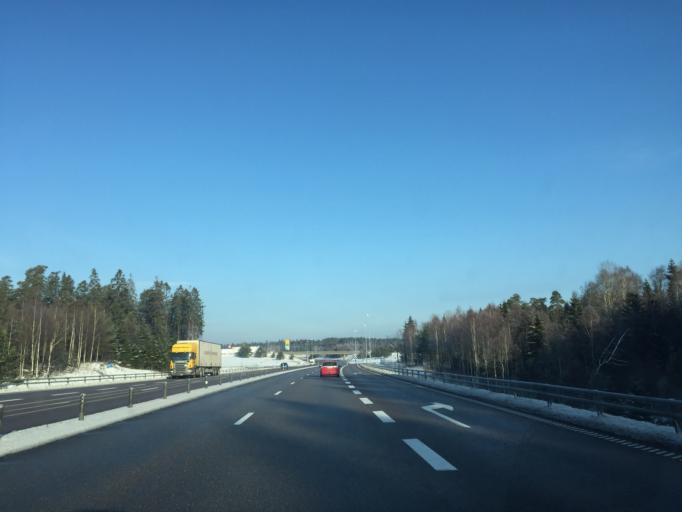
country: SE
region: Vaestra Goetaland
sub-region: Tanums Kommun
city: Tanumshede
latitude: 58.7160
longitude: 11.3542
